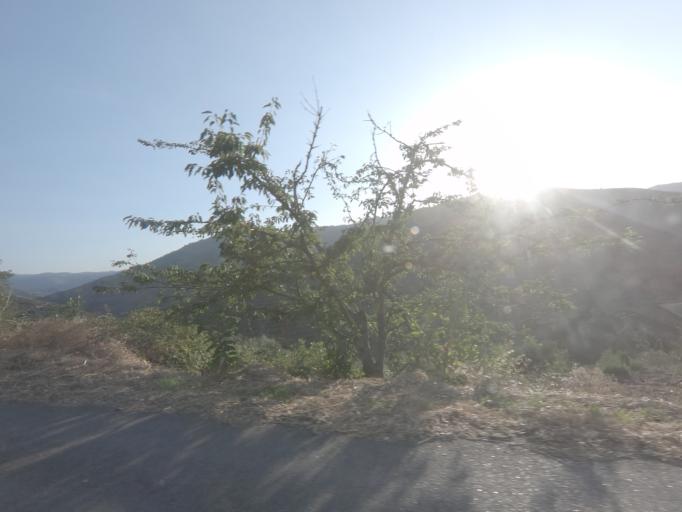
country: PT
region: Vila Real
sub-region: Sabrosa
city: Vilela
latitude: 41.1893
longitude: -7.6365
